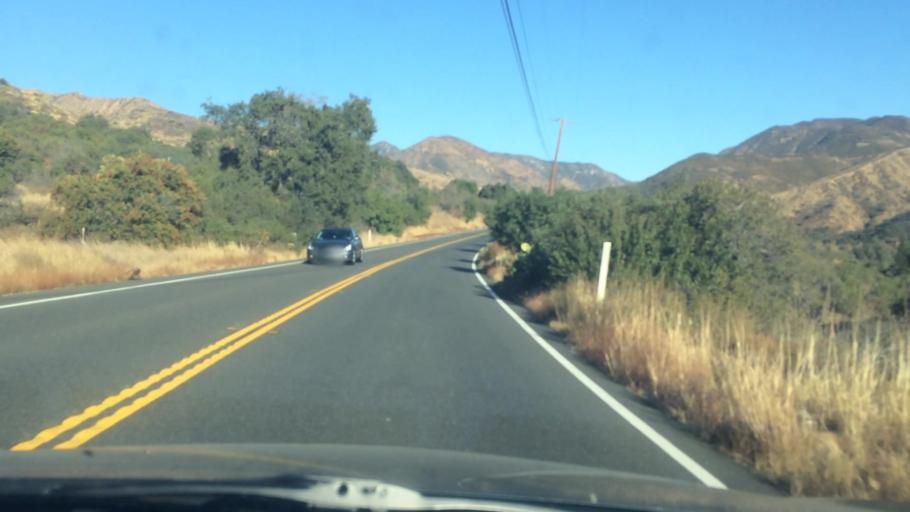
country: US
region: California
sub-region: Orange County
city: Coto De Caza
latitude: 33.5777
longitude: -117.5368
